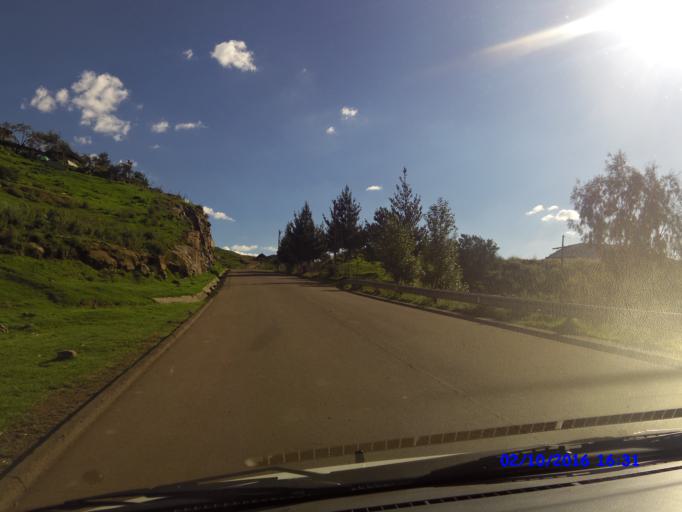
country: LS
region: Maseru
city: Nako
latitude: -29.4810
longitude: 28.0741
